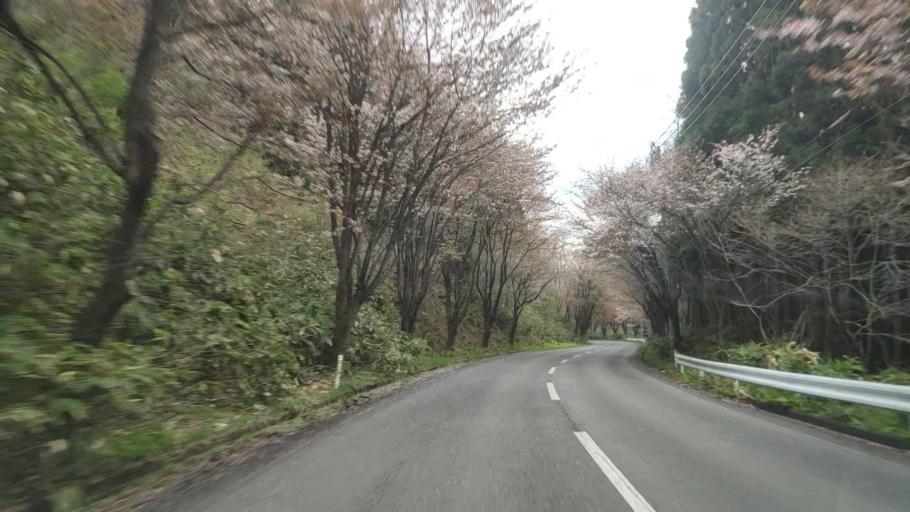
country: JP
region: Akita
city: Hanawa
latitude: 40.3624
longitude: 140.7864
